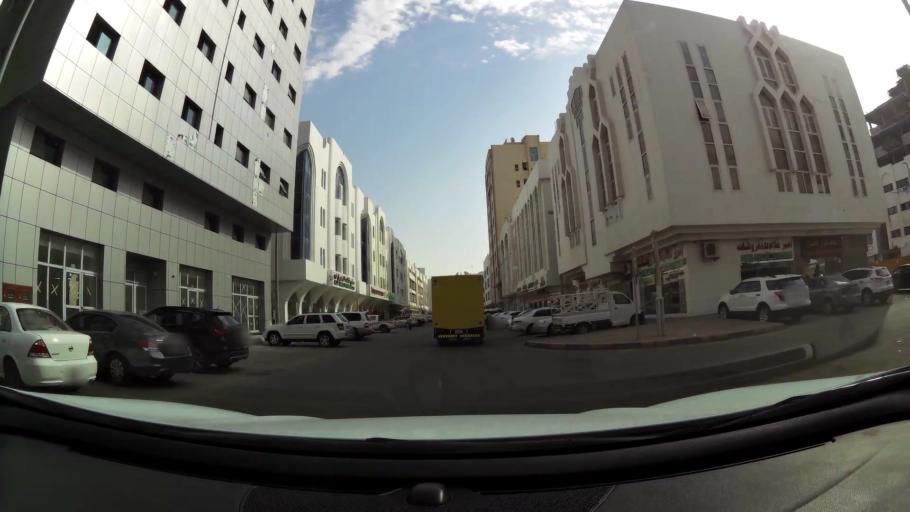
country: AE
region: Abu Dhabi
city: Abu Dhabi
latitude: 24.3238
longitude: 54.5346
